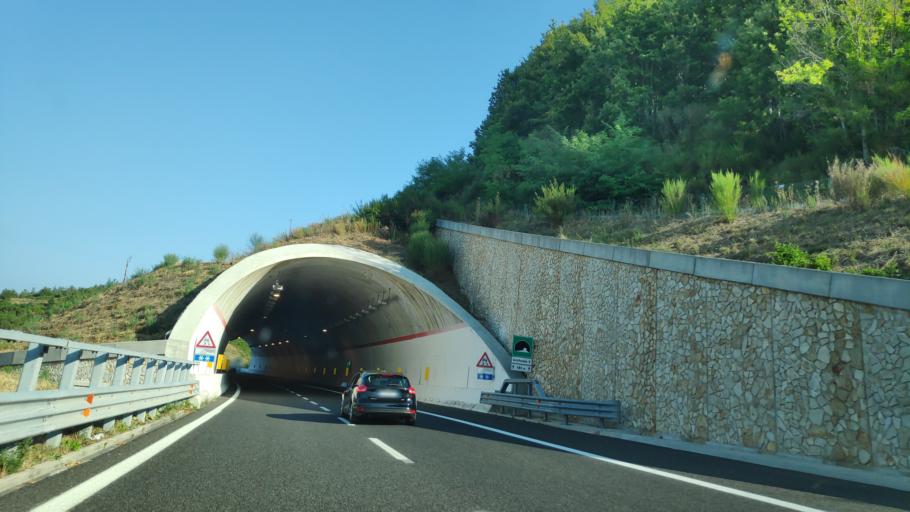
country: IT
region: Basilicate
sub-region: Provincia di Potenza
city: Lagonegro
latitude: 40.1090
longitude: 15.7936
